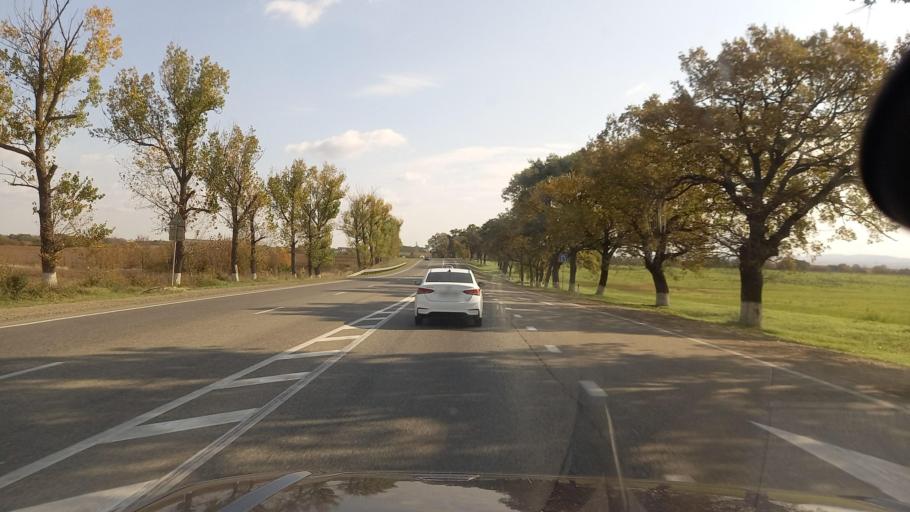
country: RU
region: Krasnodarskiy
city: Akhtyrskiy
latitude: 44.8543
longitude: 38.3382
